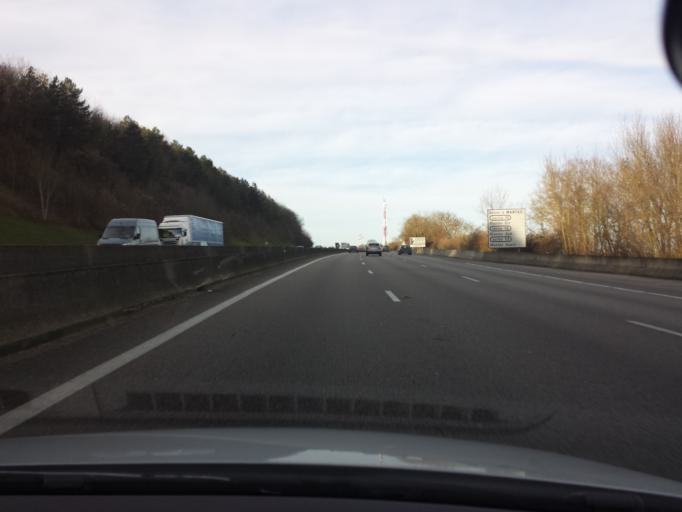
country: FR
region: Ile-de-France
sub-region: Departement des Yvelines
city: Guerville
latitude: 48.9663
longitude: 1.7488
